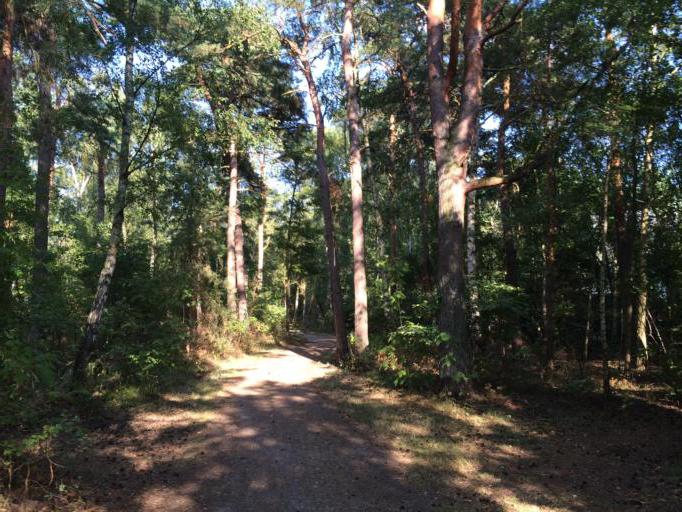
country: SE
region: Skane
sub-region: Vellinge Kommun
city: Skanor med Falsterbo
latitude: 55.4083
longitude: 12.8511
